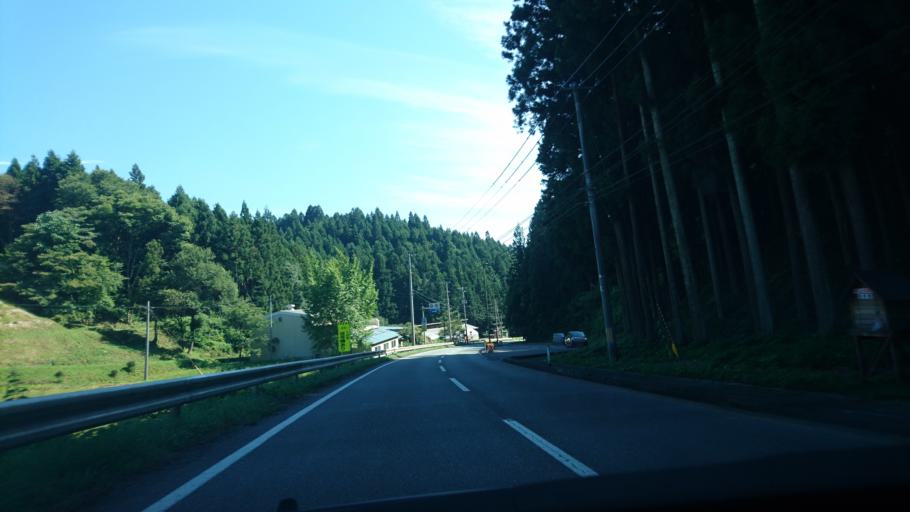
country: JP
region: Iwate
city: Ichinoseki
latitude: 38.9556
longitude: 141.1839
